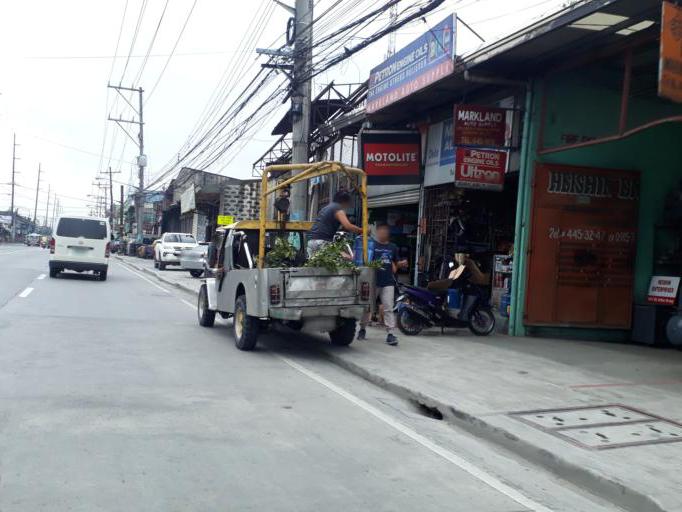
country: PH
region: Calabarzon
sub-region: Province of Rizal
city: Valenzuela
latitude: 14.7037
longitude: 120.9616
